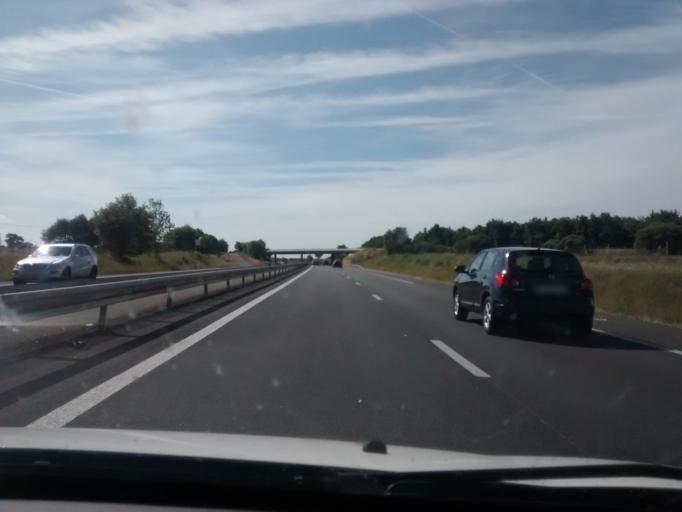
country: FR
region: Pays de la Loire
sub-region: Departement de la Mayenne
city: Sainte-Suzanne
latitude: 48.0319
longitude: -0.3535
